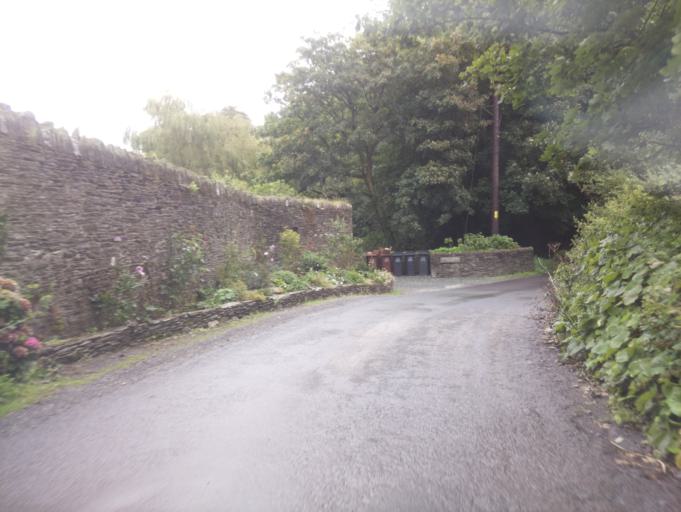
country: GB
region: England
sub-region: Devon
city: Kingsbridge
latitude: 50.3218
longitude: -3.7141
